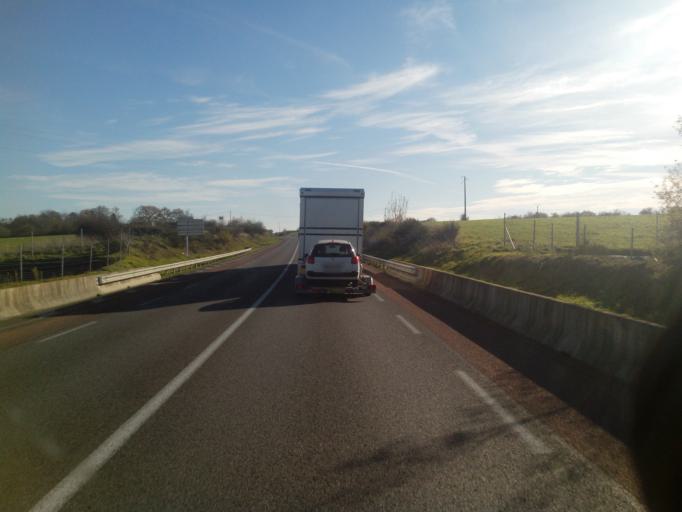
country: FR
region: Limousin
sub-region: Departement de la Haute-Vienne
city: Bellac
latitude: 46.1282
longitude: 1.0717
